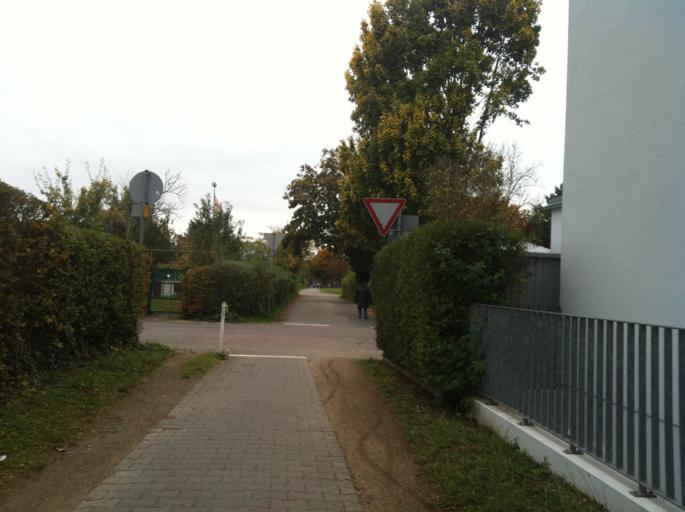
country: DE
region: Rheinland-Pfalz
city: Mainz
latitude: 49.9845
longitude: 8.2714
